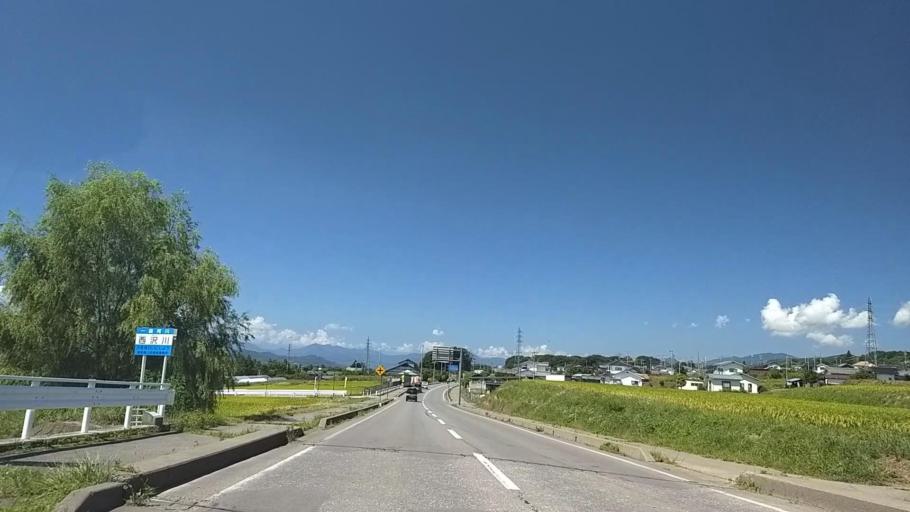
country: JP
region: Nagano
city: Komoro
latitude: 36.3566
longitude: 138.3723
